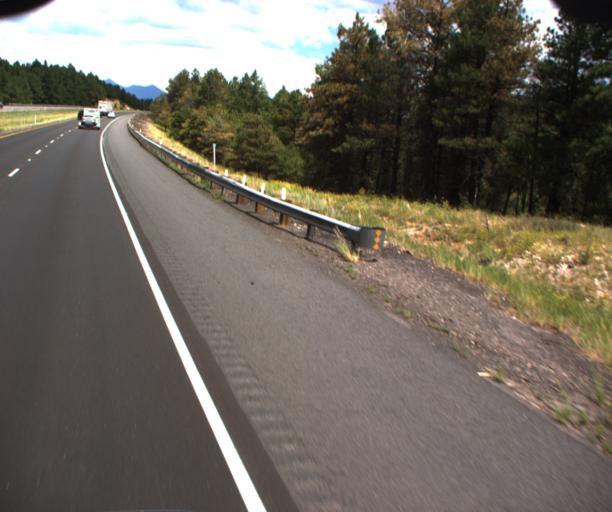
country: US
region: Arizona
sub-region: Coconino County
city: Kachina Village
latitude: 35.1109
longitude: -111.6814
